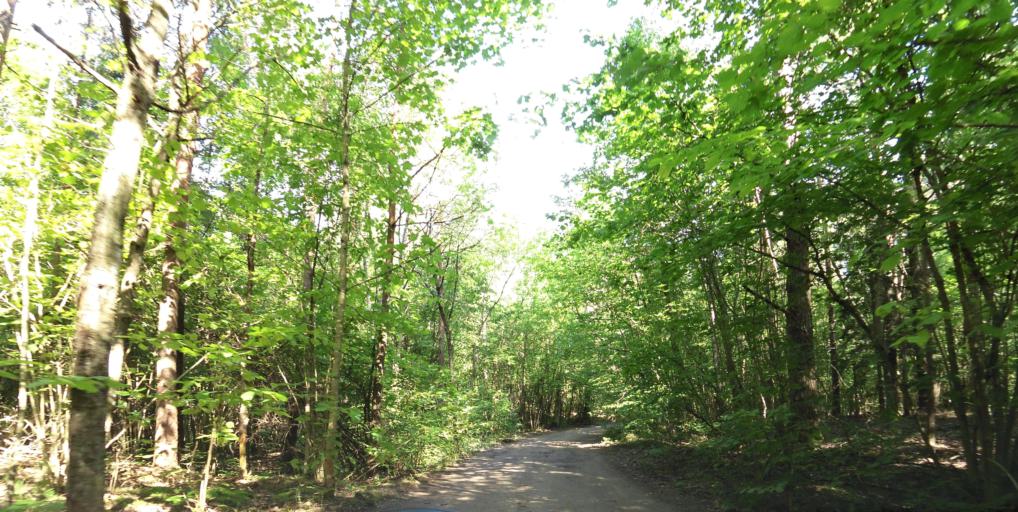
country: LT
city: Grigiskes
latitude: 54.7431
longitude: 25.0226
